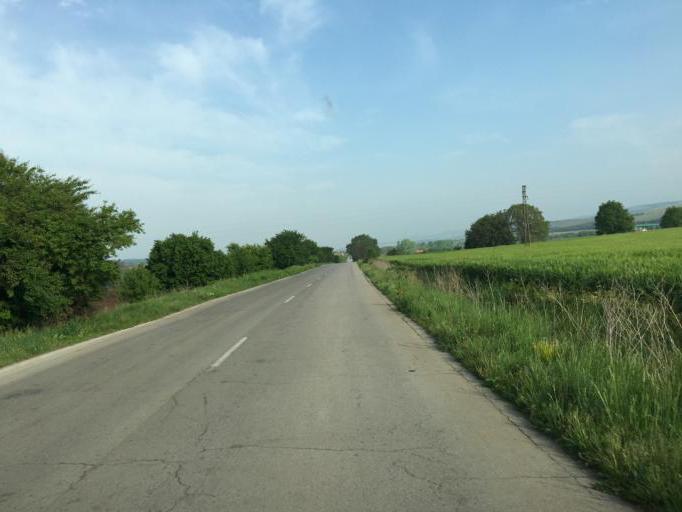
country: BG
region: Kyustendil
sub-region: Obshtina Bobovdol
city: Bobovdol
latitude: 42.4687
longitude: 23.0748
